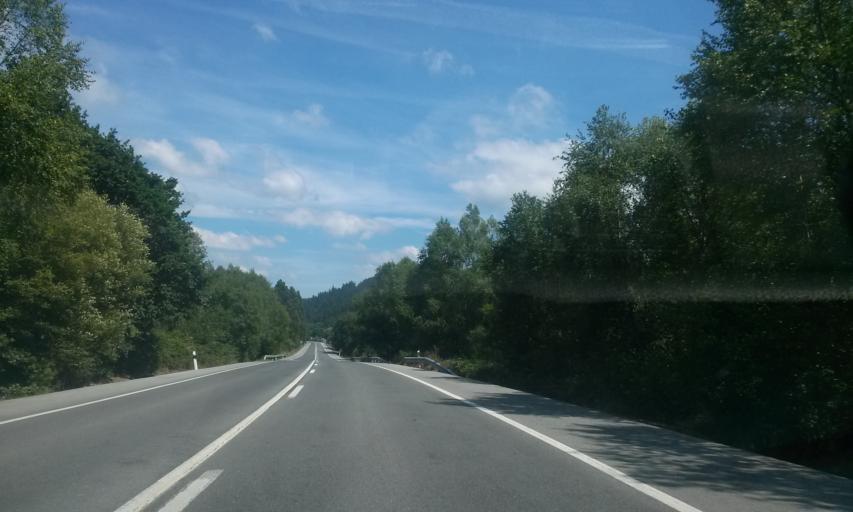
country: ES
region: Galicia
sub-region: Provincia de Lugo
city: Guitiriz
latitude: 43.1751
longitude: -7.8024
